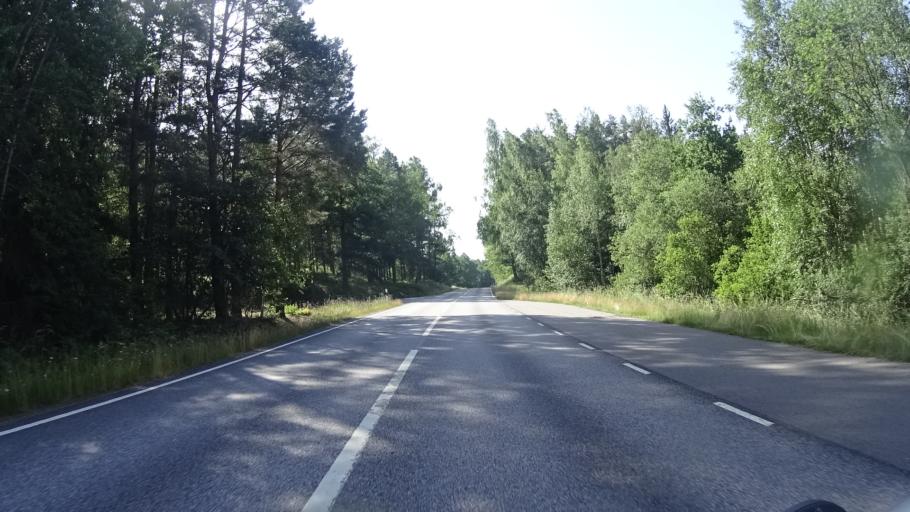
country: SE
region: Kalmar
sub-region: Vasterviks Kommun
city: Overum
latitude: 58.0426
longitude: 16.2215
